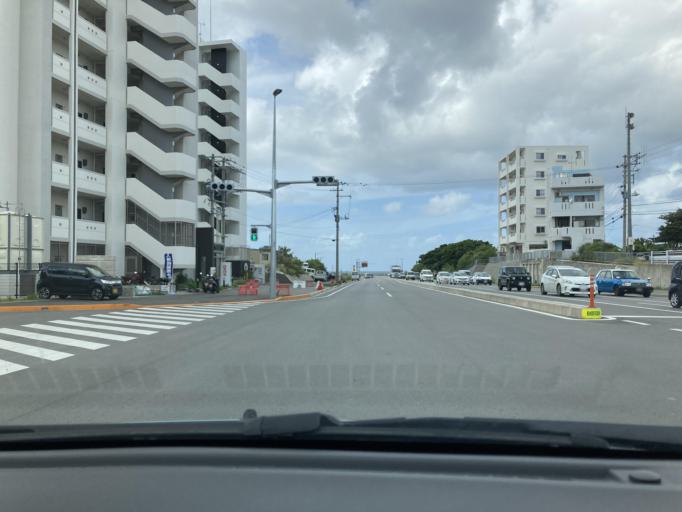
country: JP
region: Okinawa
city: Ginowan
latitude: 26.2693
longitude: 127.7091
